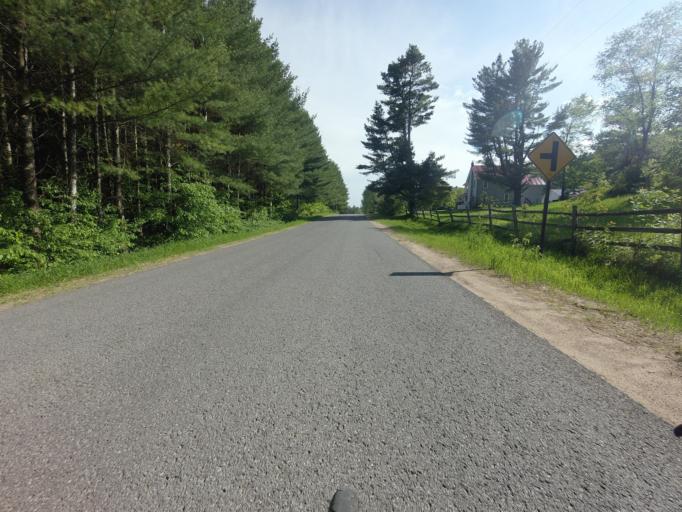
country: US
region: New York
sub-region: St. Lawrence County
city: Gouverneur
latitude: 44.2149
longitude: -75.2422
